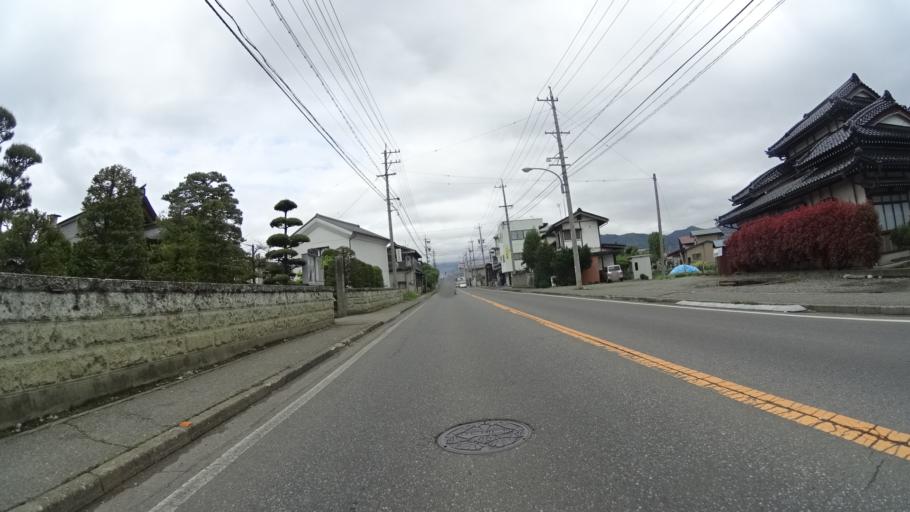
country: JP
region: Nagano
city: Nakano
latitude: 36.7414
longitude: 138.3417
